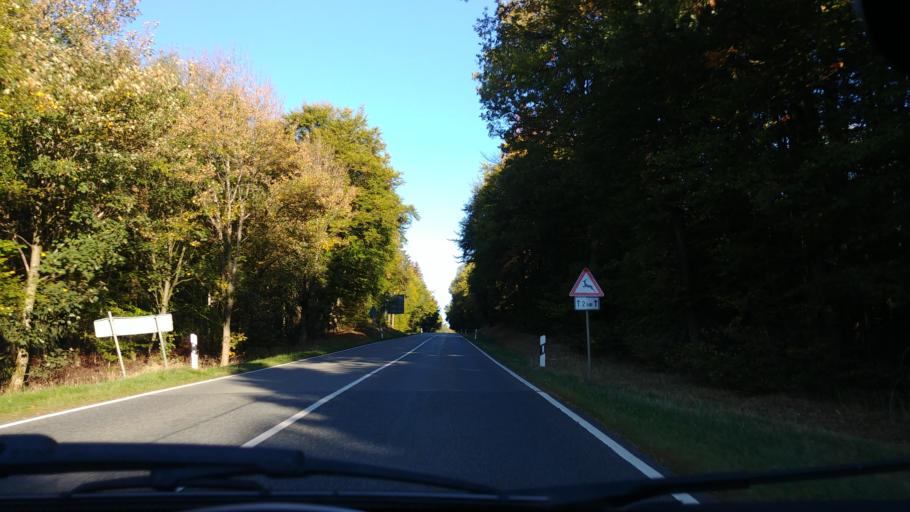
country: DE
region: Rheinland-Pfalz
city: Berndroth
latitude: 50.1878
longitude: 7.9683
